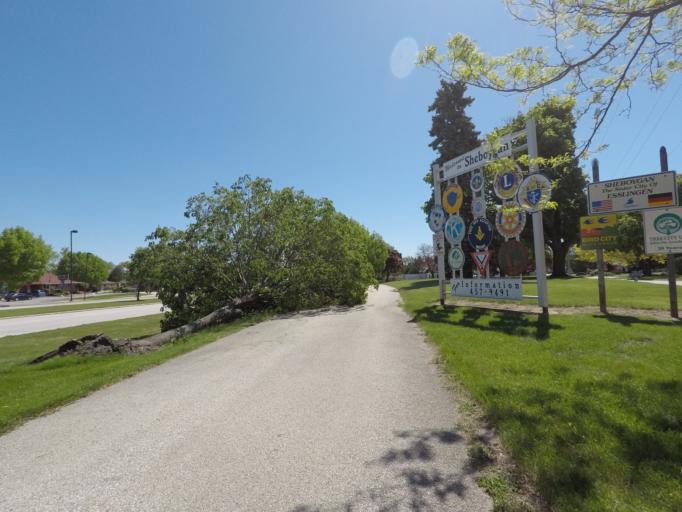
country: US
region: Wisconsin
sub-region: Sheboygan County
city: Sheboygan
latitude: 43.7562
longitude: -87.7459
